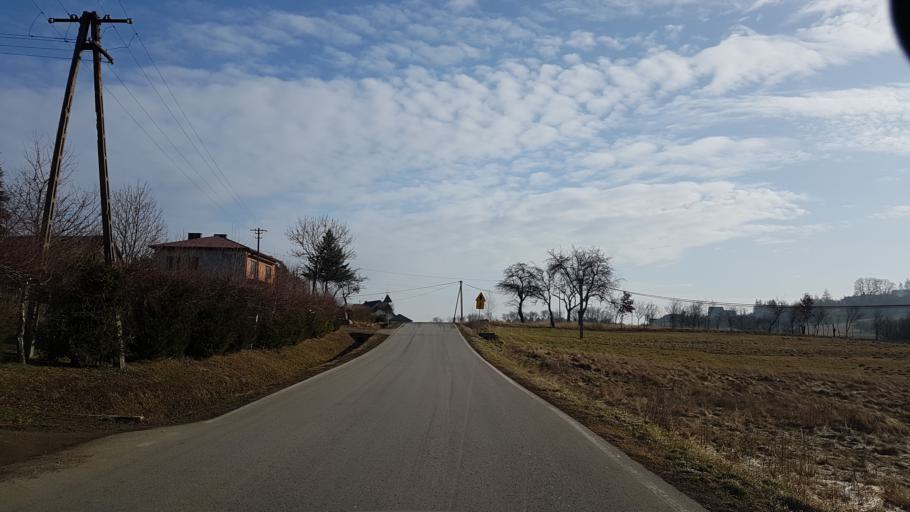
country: PL
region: Lesser Poland Voivodeship
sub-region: Powiat limanowski
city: Lukowica
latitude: 49.6351
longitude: 20.5195
